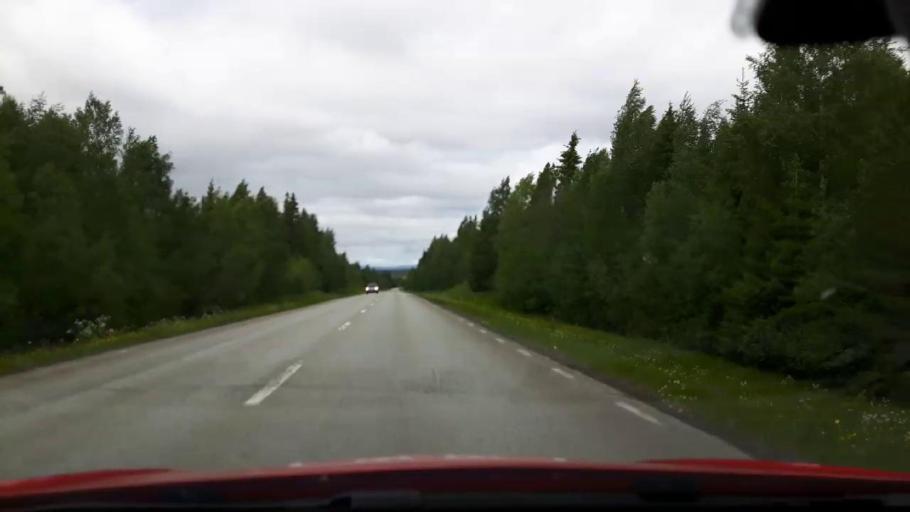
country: SE
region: Jaemtland
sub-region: Krokoms Kommun
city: Krokom
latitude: 63.3926
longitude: 14.5027
